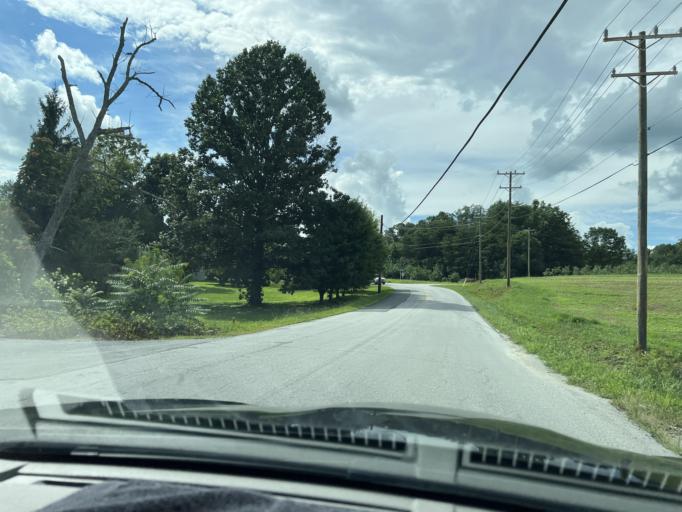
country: US
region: North Carolina
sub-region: Henderson County
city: Edneyville
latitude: 35.3882
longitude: -82.3530
